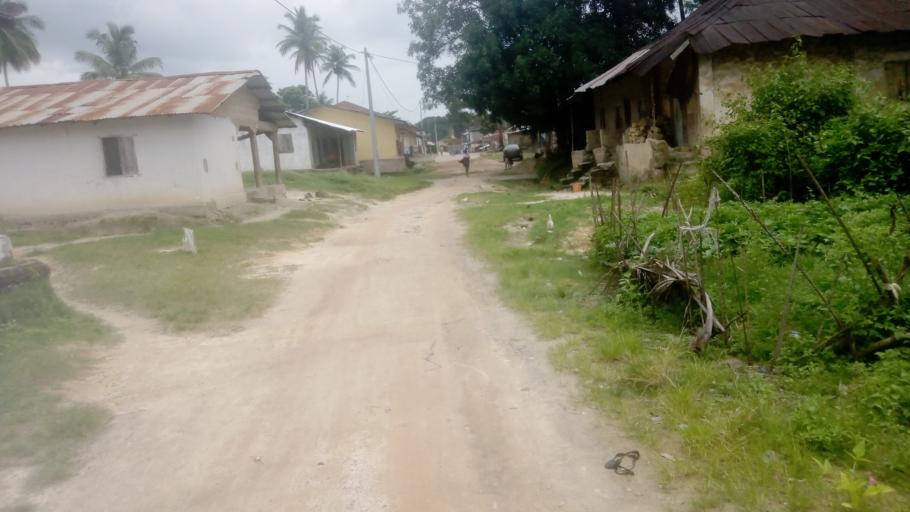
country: SL
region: Northern Province
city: Lunsar
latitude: 8.6791
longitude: -12.5345
